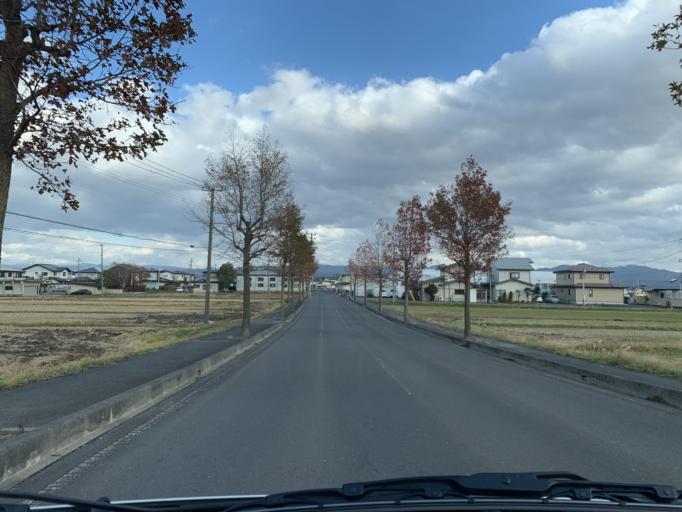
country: JP
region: Iwate
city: Mizusawa
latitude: 39.1347
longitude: 141.1224
